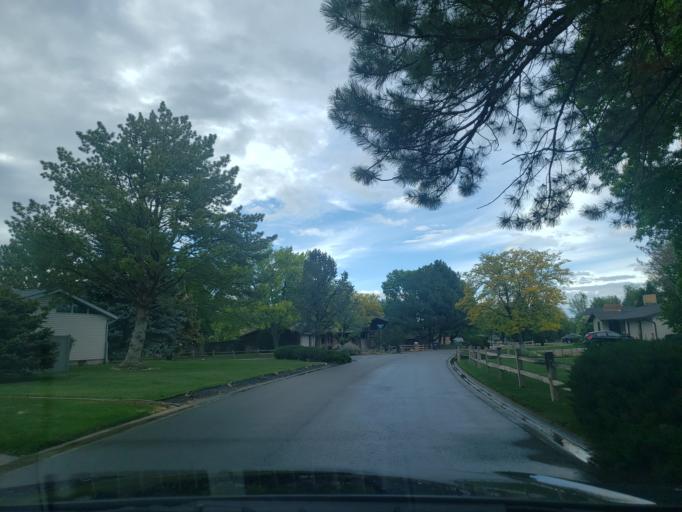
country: US
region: Colorado
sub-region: Mesa County
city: Redlands
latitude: 39.0934
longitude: -108.6530
